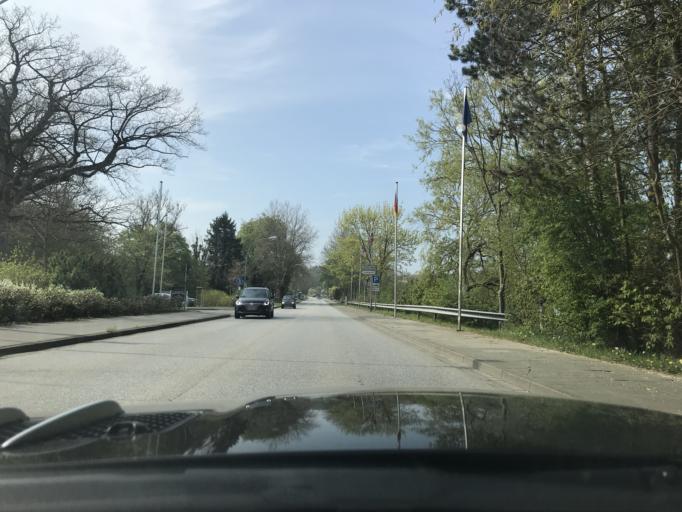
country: DE
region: Schleswig-Holstein
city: Riepsdorf
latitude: 54.1906
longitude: 10.9845
